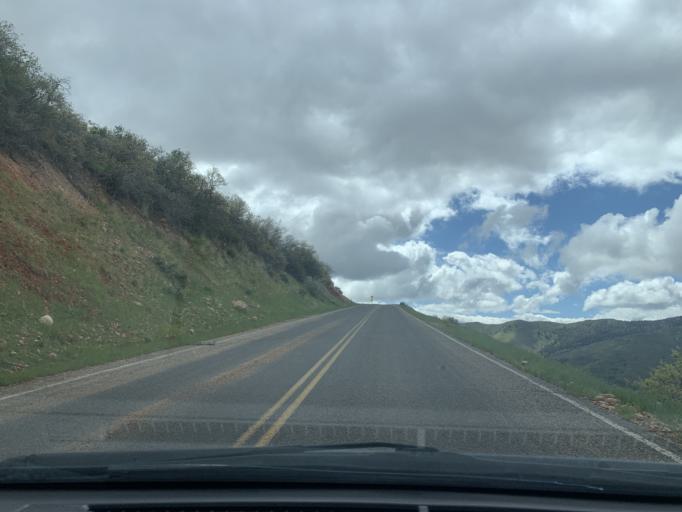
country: US
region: Utah
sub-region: Sanpete County
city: Fountain Green
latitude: 39.7854
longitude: -111.6814
